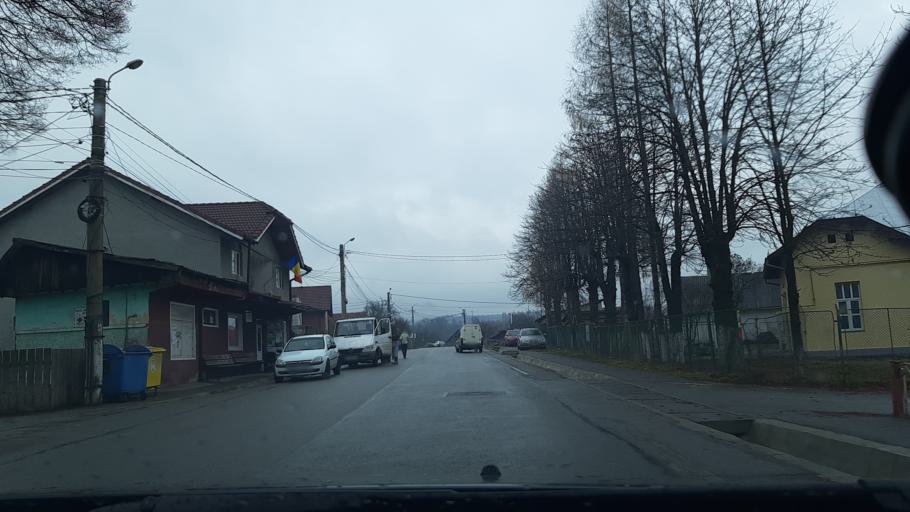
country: RO
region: Hunedoara
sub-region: Oras Petrila
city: Petrila
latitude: 45.4420
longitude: 23.4117
